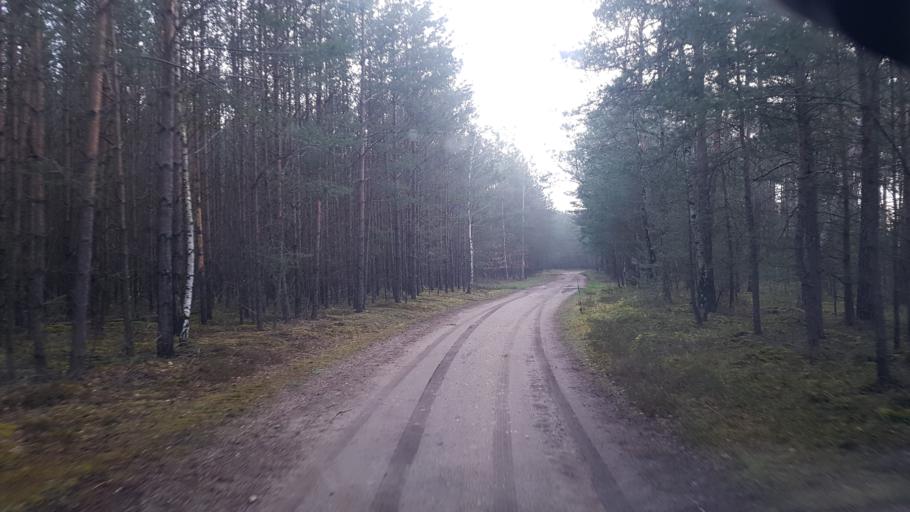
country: DE
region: Brandenburg
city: Trobitz
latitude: 51.5482
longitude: 13.4574
